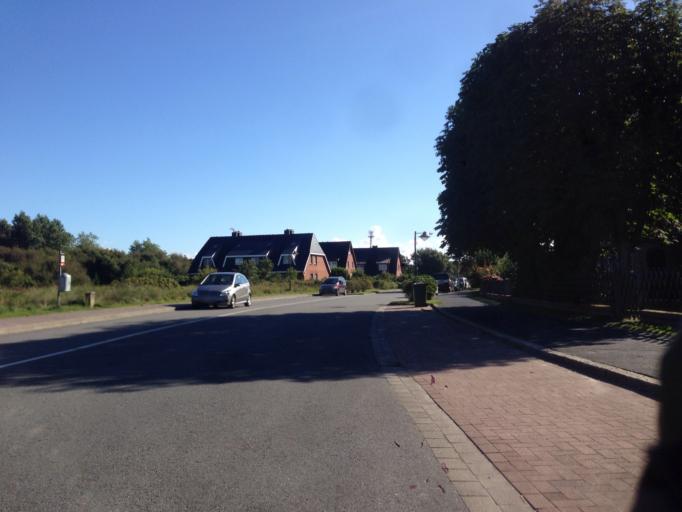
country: DE
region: Schleswig-Holstein
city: List
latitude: 55.0210
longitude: 8.4211
